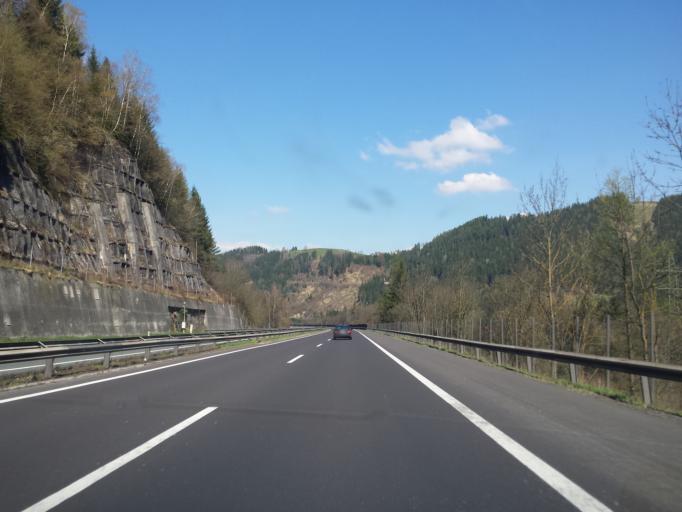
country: AT
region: Styria
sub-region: Politischer Bezirk Leoben
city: Sankt Michael in Obersteiermark
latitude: 47.3116
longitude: 15.0561
